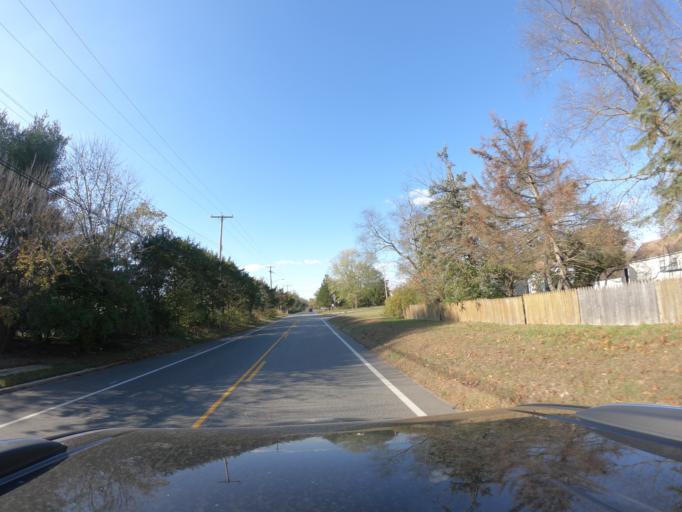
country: US
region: New Jersey
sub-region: Monmouth County
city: Ramtown
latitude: 40.0941
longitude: -74.1587
